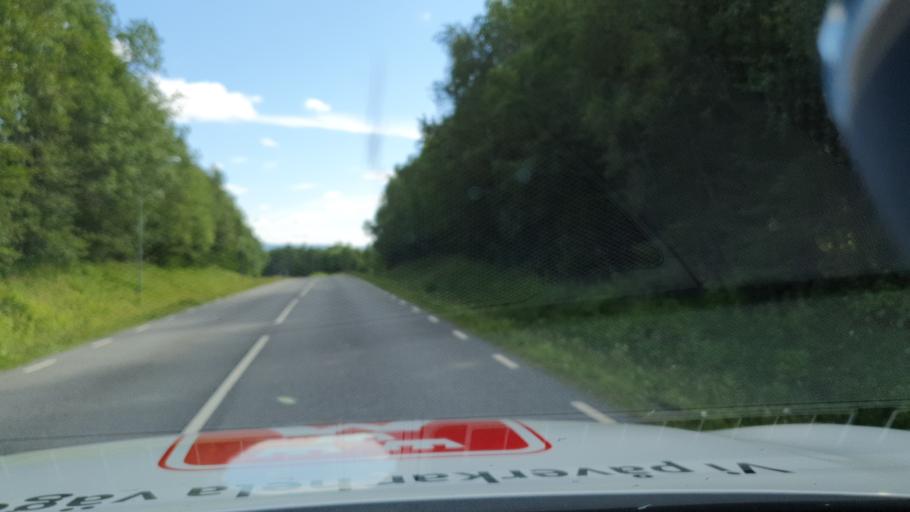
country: SE
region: Jaemtland
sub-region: Are Kommun
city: Are
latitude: 63.6877
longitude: 12.9847
